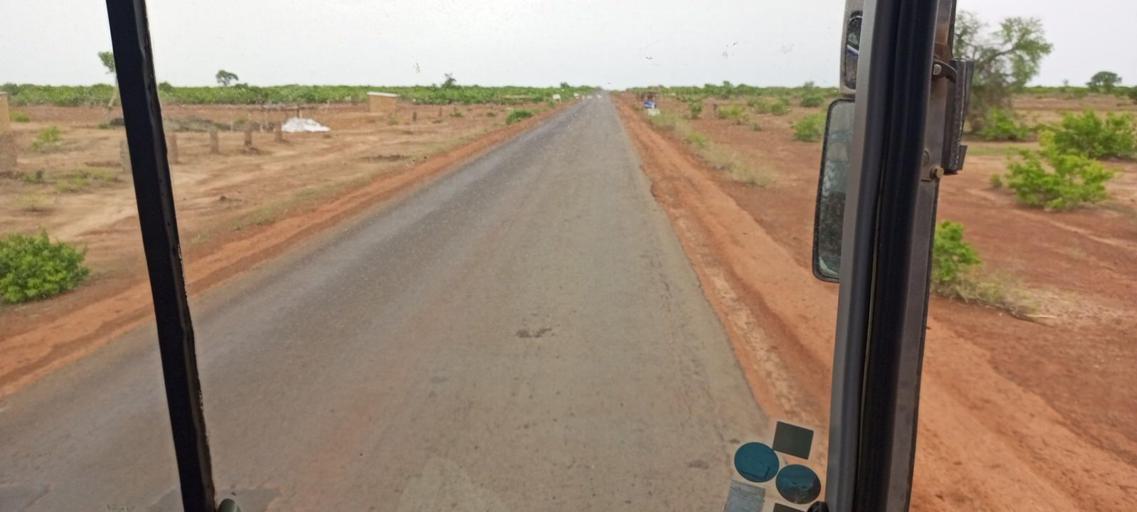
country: ML
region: Segou
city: Bla
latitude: 12.7063
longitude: -5.7243
